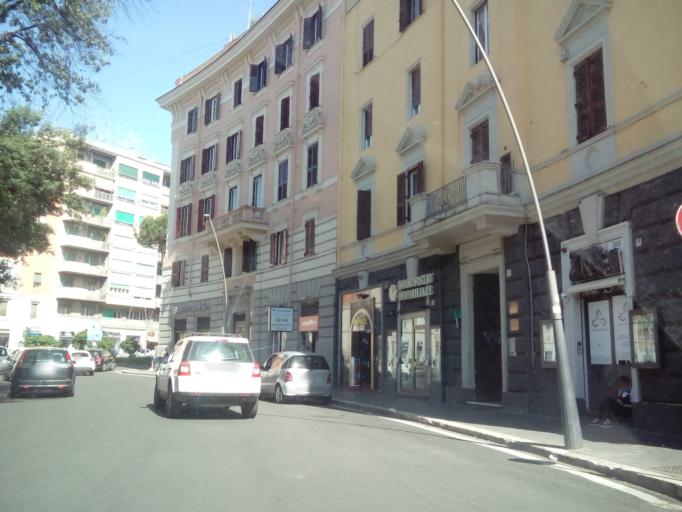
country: IT
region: Latium
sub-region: Citta metropolitana di Roma Capitale
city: Rome
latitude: 41.8812
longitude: 12.5138
